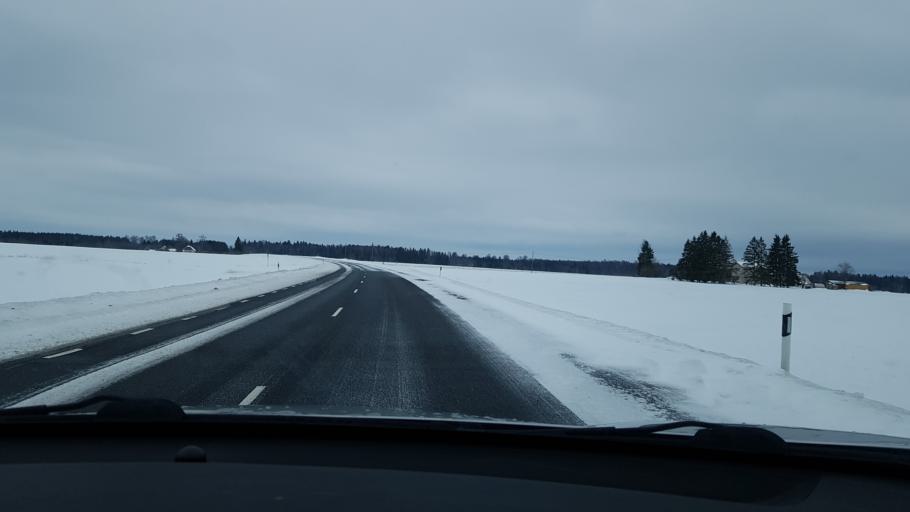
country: EE
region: Jaervamaa
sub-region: Jaerva-Jaani vald
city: Jarva-Jaani
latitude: 59.1116
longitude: 25.7967
